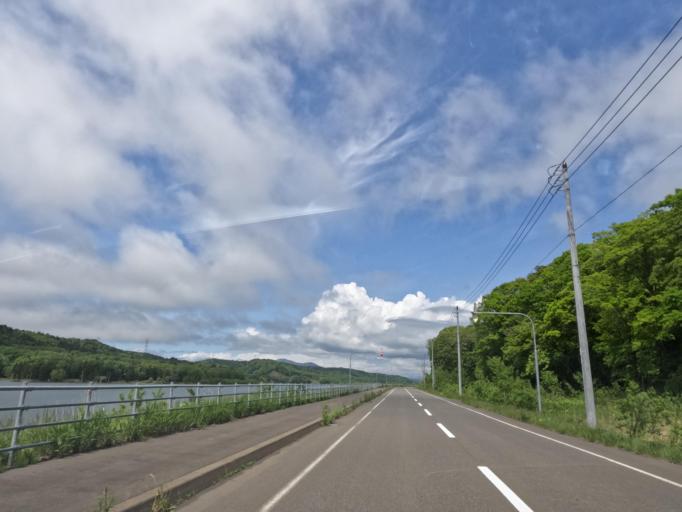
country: JP
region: Hokkaido
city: Tobetsu
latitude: 43.3588
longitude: 141.5680
